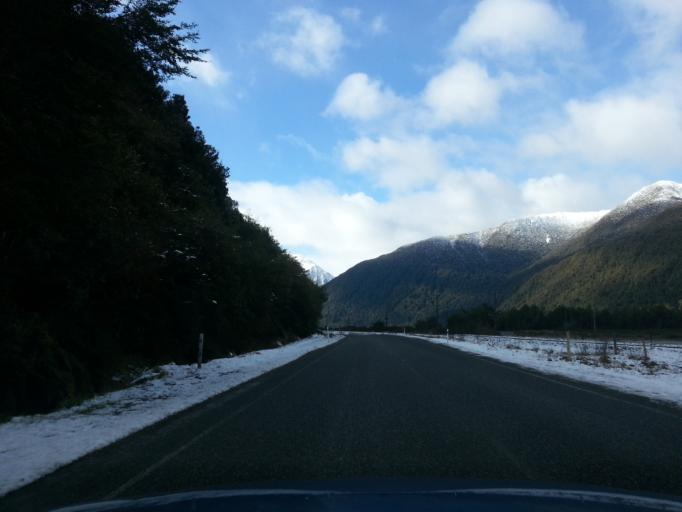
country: NZ
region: West Coast
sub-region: Grey District
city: Greymouth
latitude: -42.7904
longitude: 171.5978
